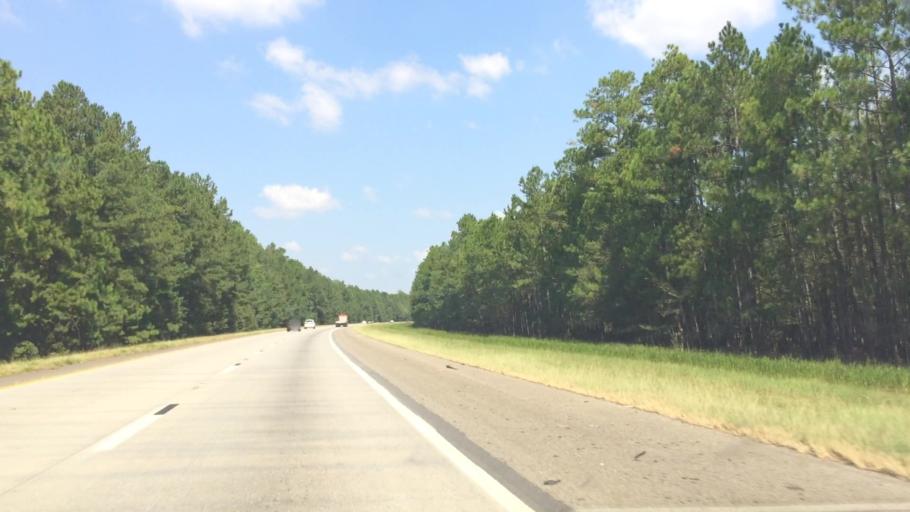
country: US
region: South Carolina
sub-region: Colleton County
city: Walterboro
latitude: 33.0421
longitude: -80.6692
